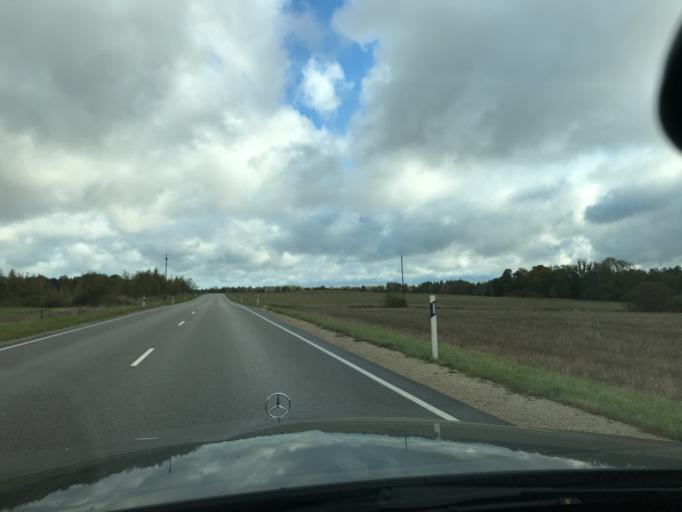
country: EE
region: Valgamaa
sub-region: Torva linn
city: Torva
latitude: 58.0127
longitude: 25.7946
